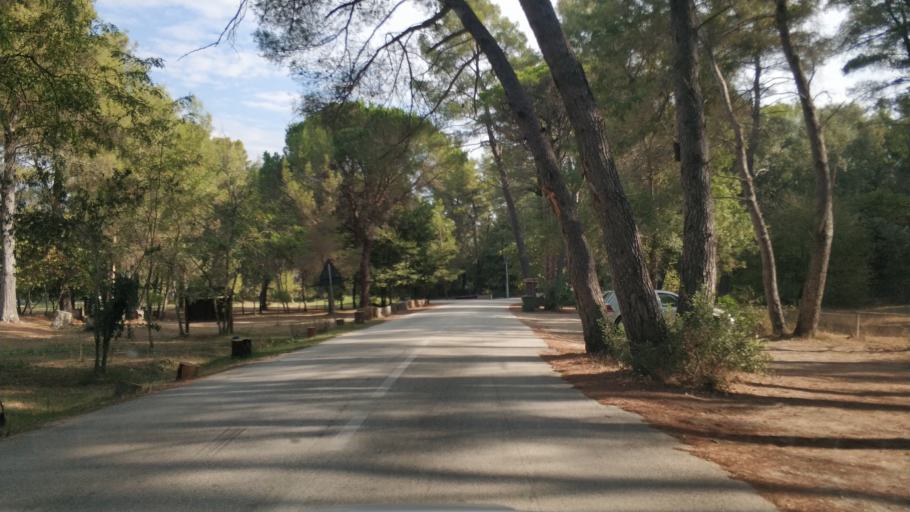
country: AL
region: Fier
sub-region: Rrethi i Lushnjes
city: Divjake
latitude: 40.9892
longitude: 19.4851
